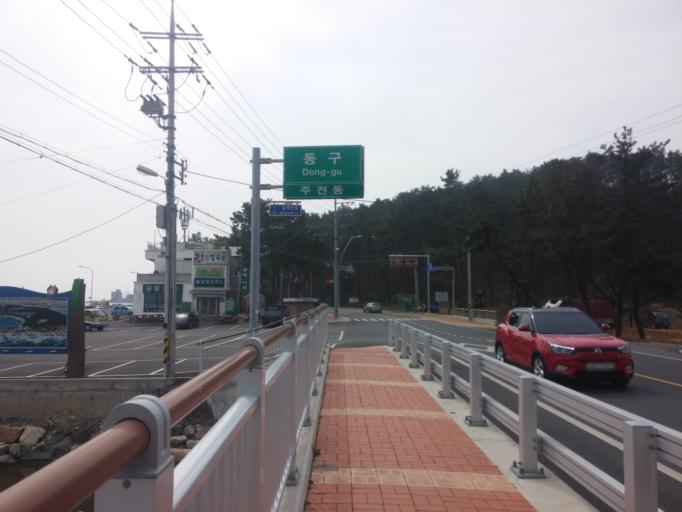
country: KR
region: Ulsan
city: Ulsan
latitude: 35.5720
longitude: 129.4519
